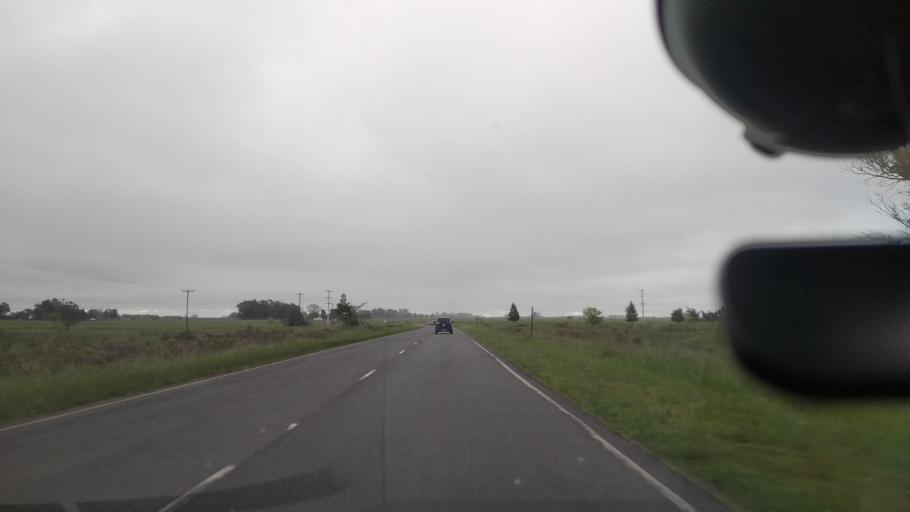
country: AR
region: Buenos Aires
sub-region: Partido de Magdalena
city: Magdalena
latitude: -35.2214
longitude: -57.7357
